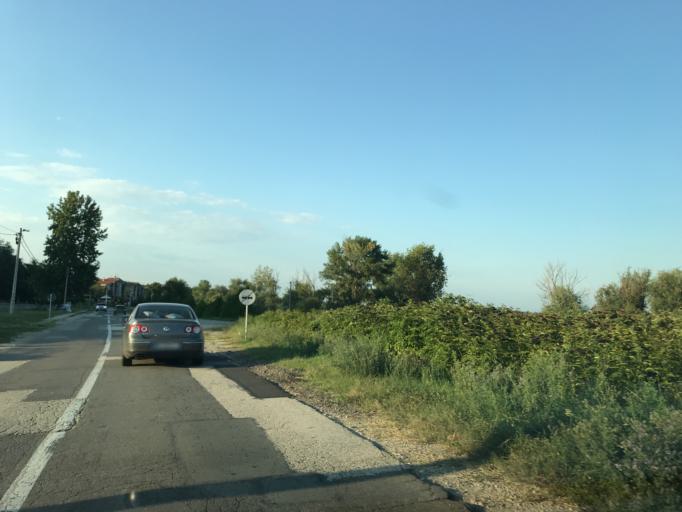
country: RO
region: Mehedinti
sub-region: Comuna Gogosu
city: Ostrovu Mare
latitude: 44.4790
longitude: 22.4532
